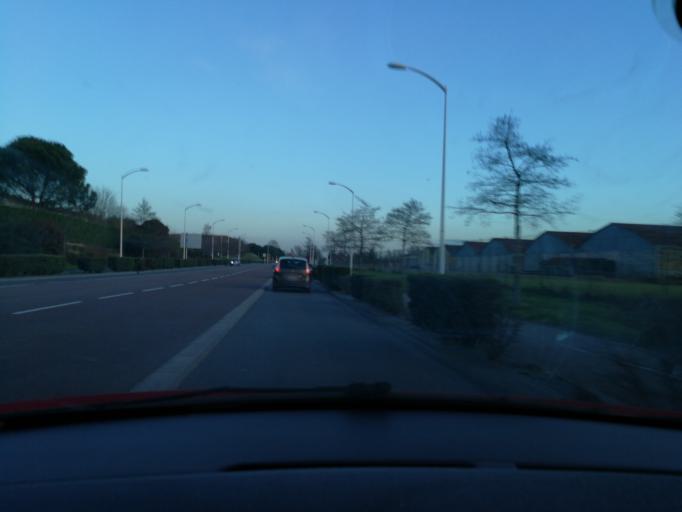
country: FR
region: Midi-Pyrenees
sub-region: Departement de la Haute-Garonne
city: Balma
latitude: 43.6086
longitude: 1.4906
